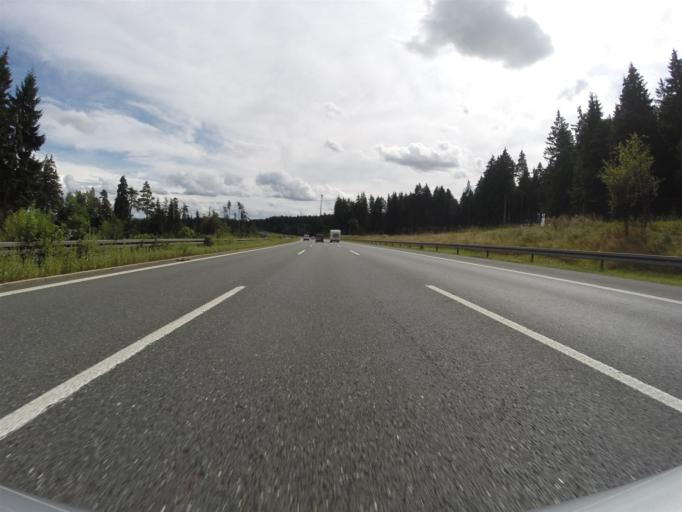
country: DE
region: Bavaria
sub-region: Upper Franconia
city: Munchberg
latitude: 50.2342
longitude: 11.7769
